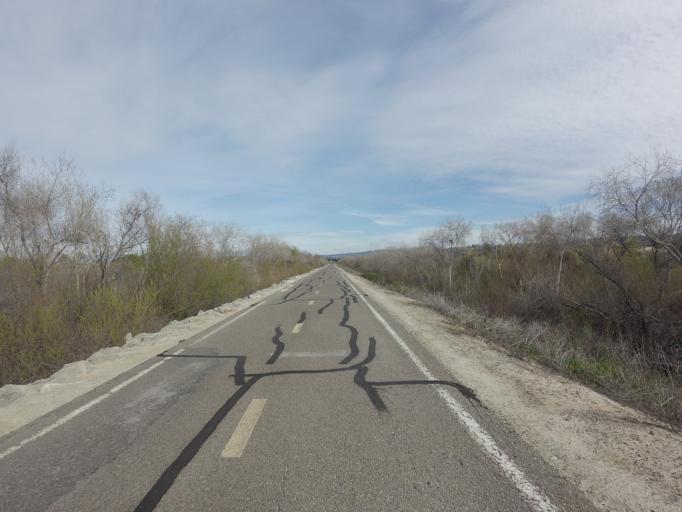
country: US
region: California
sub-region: San Diego County
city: Camp Pendleton South
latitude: 33.2398
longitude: -117.3179
